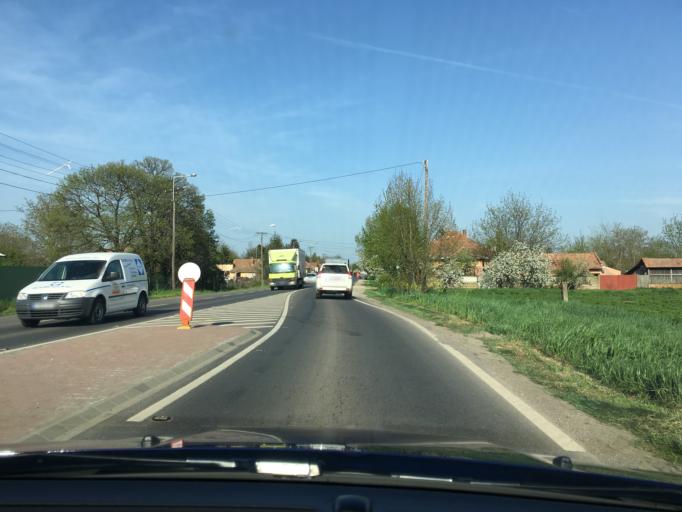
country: HU
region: Bekes
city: Csorvas
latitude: 46.6296
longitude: 20.8170
